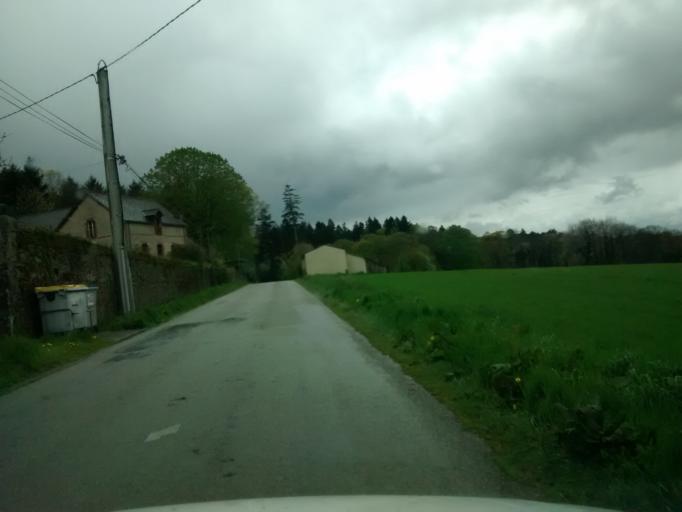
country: FR
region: Brittany
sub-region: Departement du Morbihan
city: Pleucadeuc
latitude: 47.7607
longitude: -2.3482
